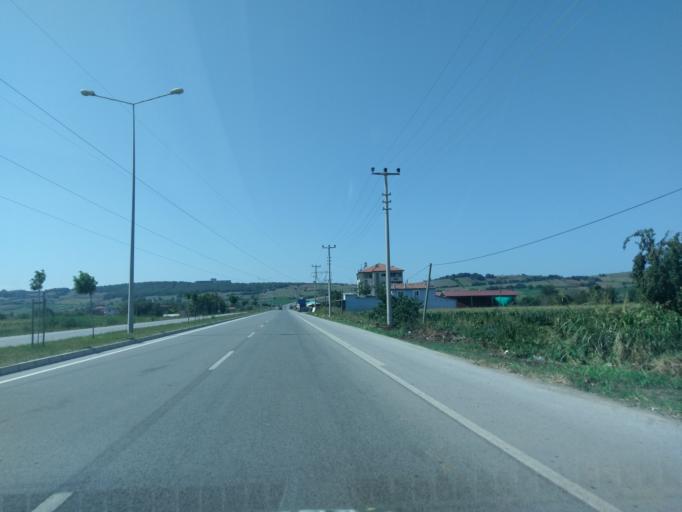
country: TR
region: Samsun
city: Bafra
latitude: 41.5762
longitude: 35.8579
